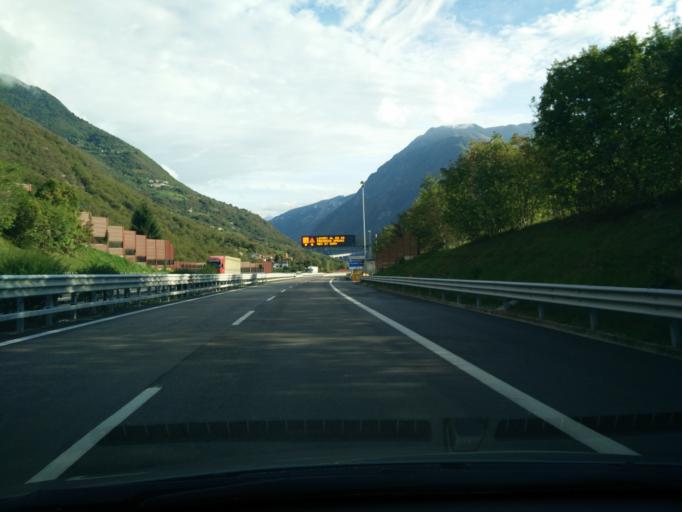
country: IT
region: Veneto
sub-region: Provincia di Treviso
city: Revine
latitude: 46.0125
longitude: 12.2794
